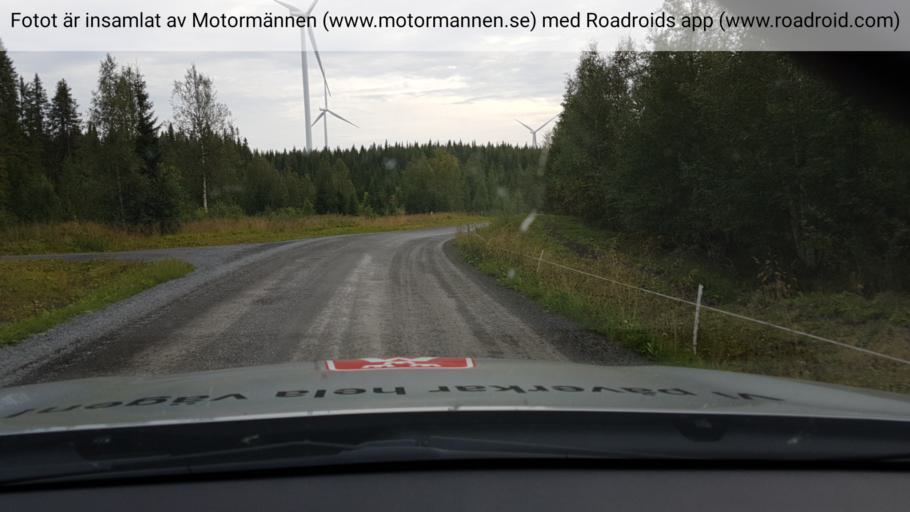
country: SE
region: Jaemtland
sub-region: OEstersunds Kommun
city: Lit
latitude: 63.6013
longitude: 14.9969
